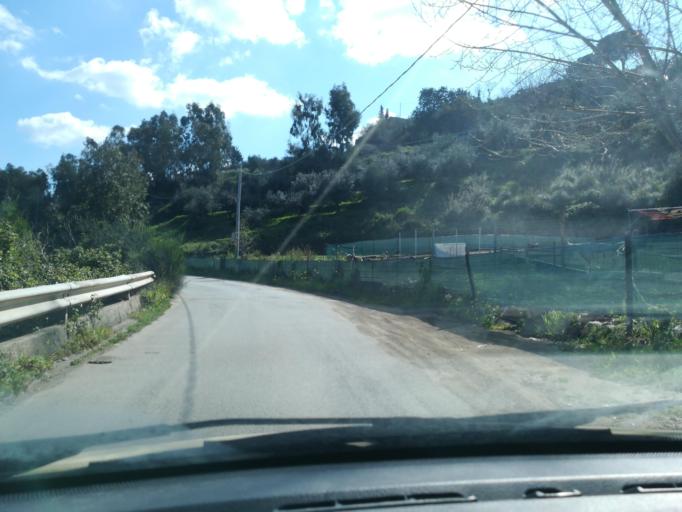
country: IT
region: Sicily
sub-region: Palermo
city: Altofonte
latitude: 38.0433
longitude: 13.2765
